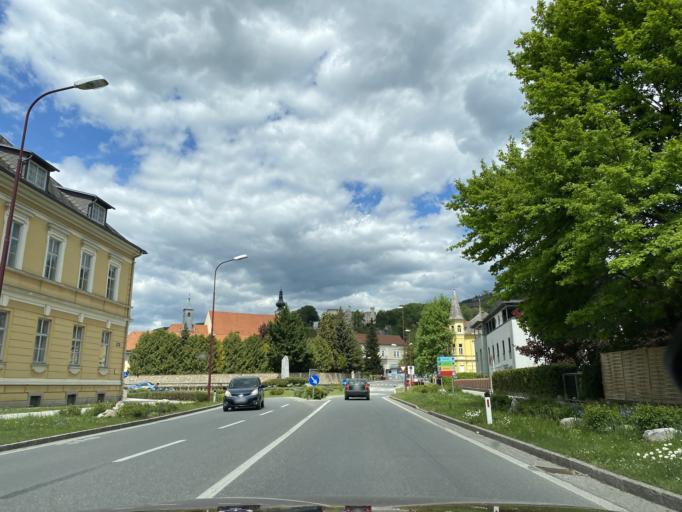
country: AT
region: Carinthia
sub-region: Politischer Bezirk Wolfsberg
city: Wolfsberg
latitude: 46.8351
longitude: 14.8439
